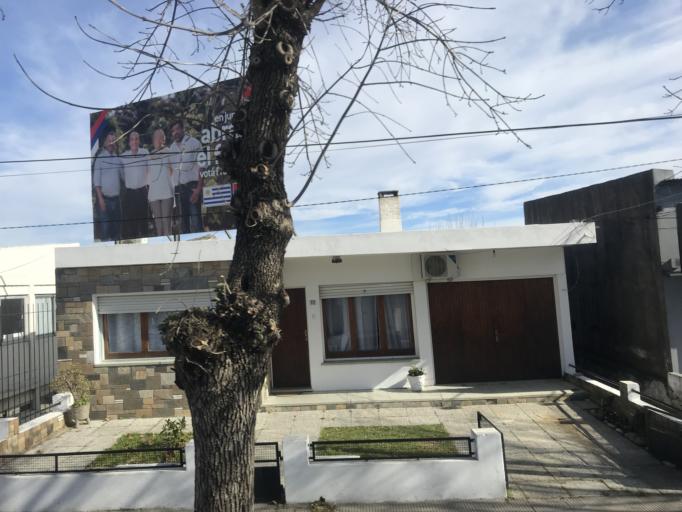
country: UY
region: Colonia
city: Colonia del Sacramento
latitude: -34.4642
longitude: -57.8385
